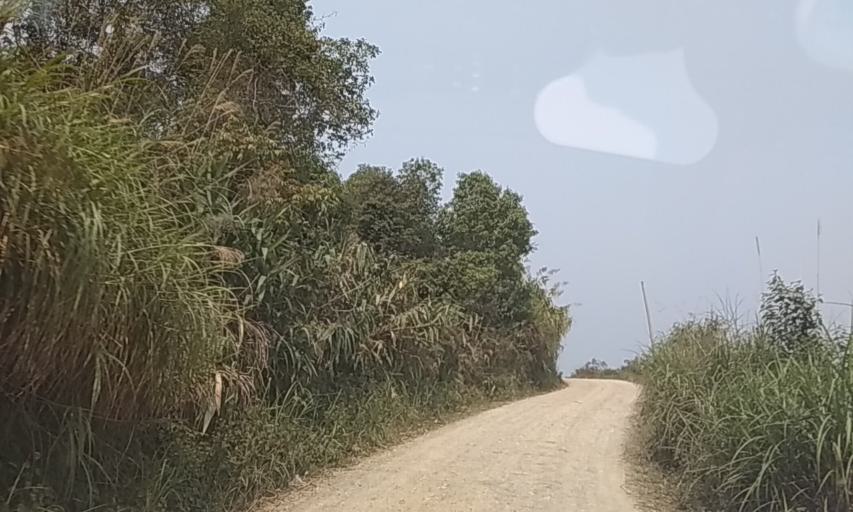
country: TH
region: Nan
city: Chaloem Phra Kiat
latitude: 20.0513
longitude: 101.0743
